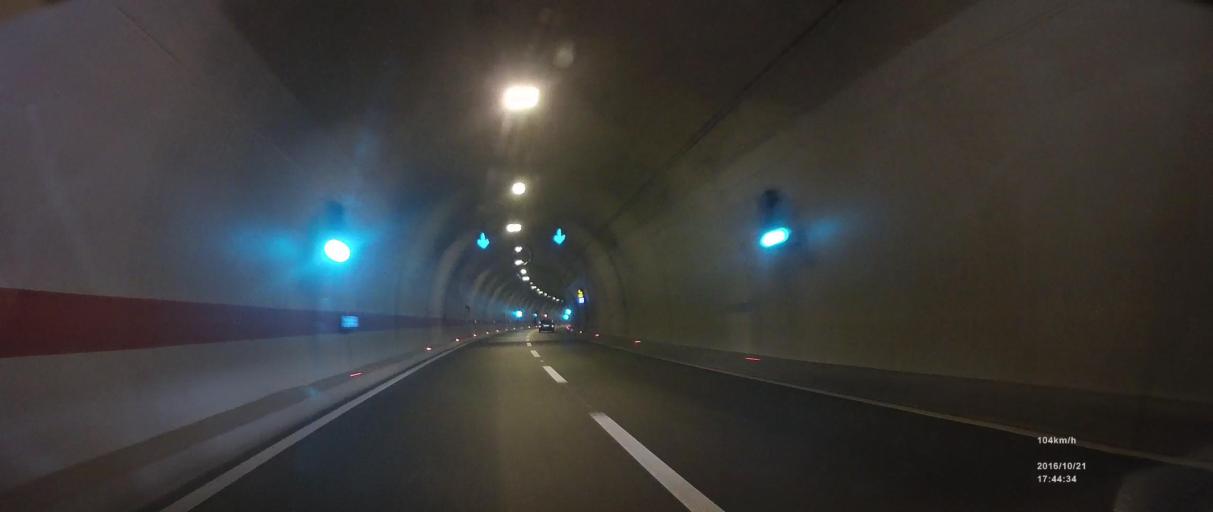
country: HR
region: Primorsko-Goranska
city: Hreljin
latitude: 45.2814
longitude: 14.5917
